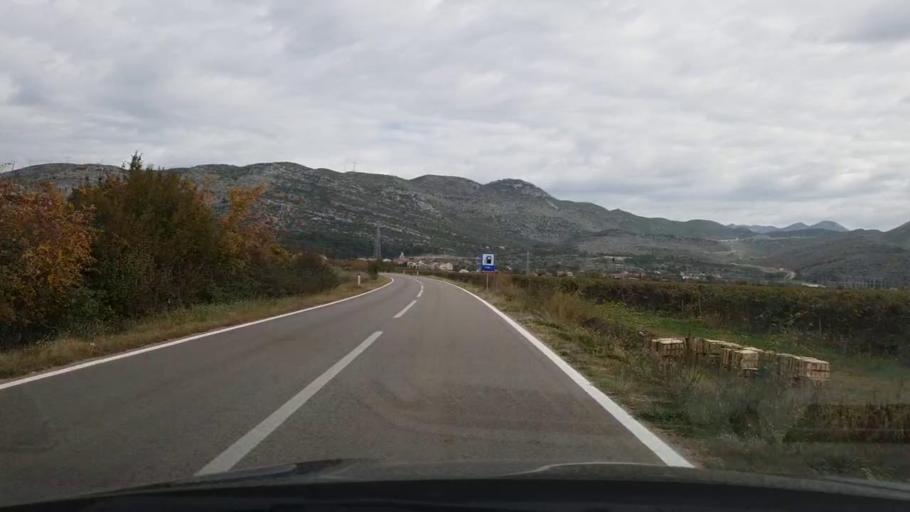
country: BA
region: Republika Srpska
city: Trebinje
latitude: 42.6854
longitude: 18.3191
